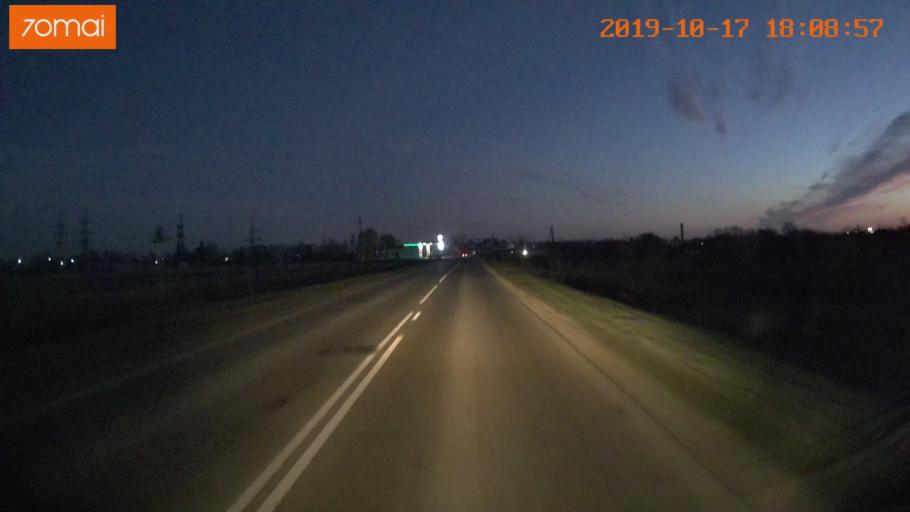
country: RU
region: Tula
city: Kurkino
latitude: 53.4280
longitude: 38.6449
